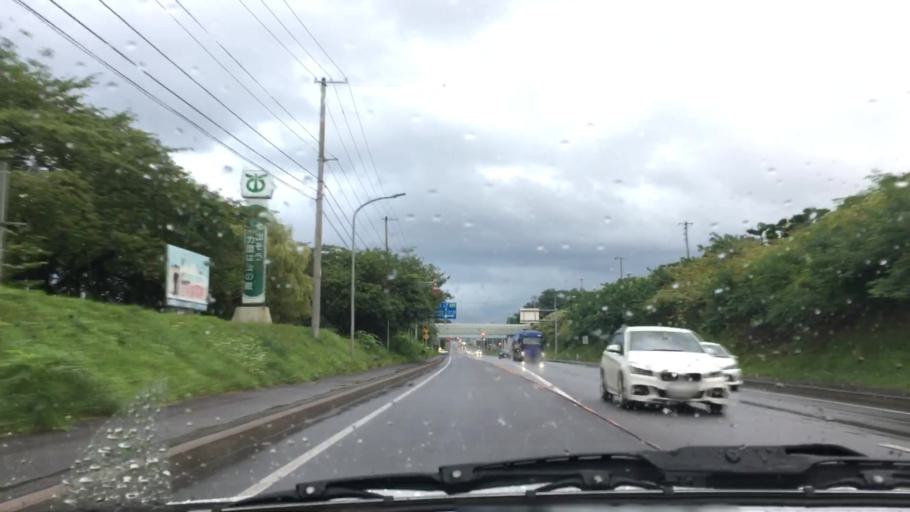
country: JP
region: Hokkaido
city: Nanae
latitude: 42.0985
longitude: 140.5685
